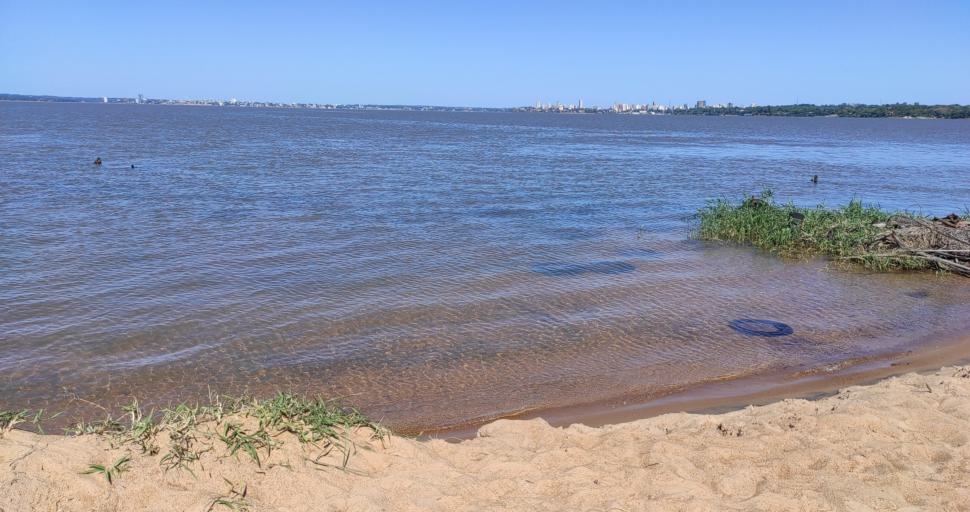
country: PY
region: Itapua
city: San Juan del Parana
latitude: -27.3401
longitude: -55.9497
